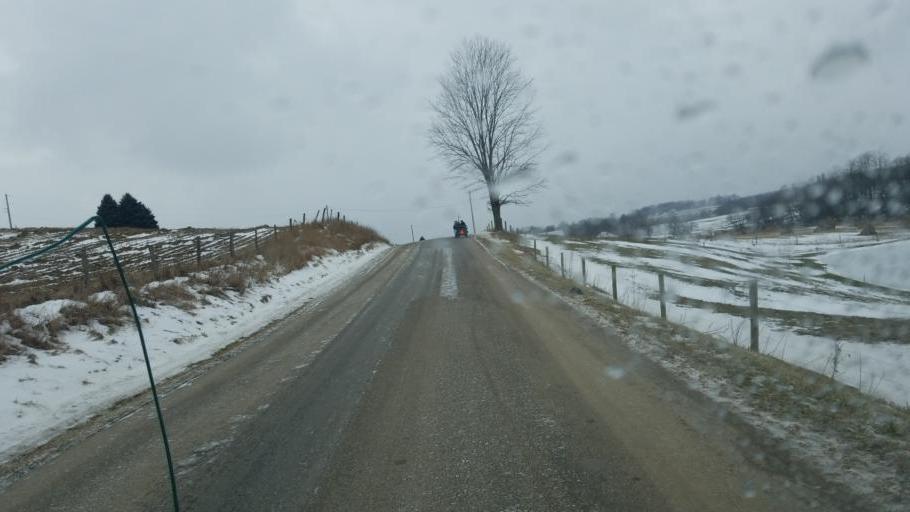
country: US
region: Ohio
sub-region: Wayne County
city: Apple Creek
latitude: 40.6753
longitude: -81.7992
